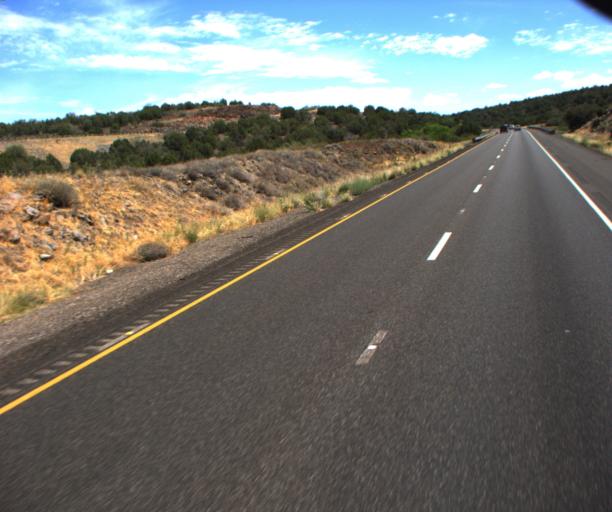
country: US
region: Arizona
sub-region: Yavapai County
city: Big Park
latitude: 34.7220
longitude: -111.7164
